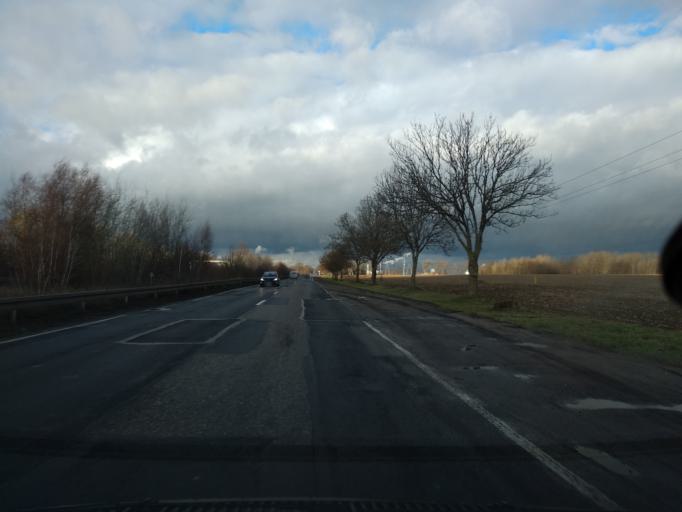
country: PL
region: Greater Poland Voivodeship
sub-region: Konin
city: Konin
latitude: 52.2557
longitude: 18.2689
